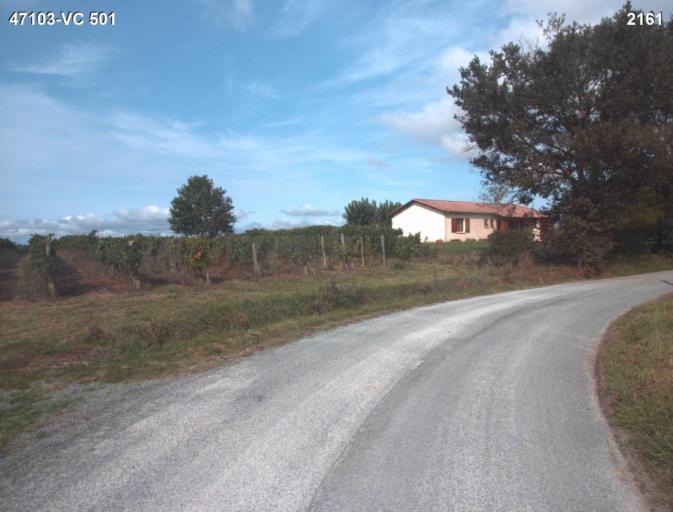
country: FR
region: Aquitaine
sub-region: Departement du Lot-et-Garonne
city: Nerac
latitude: 44.0971
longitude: 0.3278
